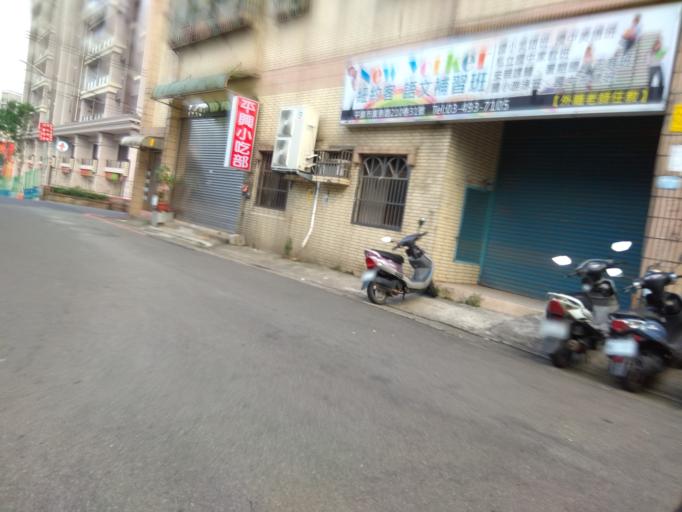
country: TW
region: Taiwan
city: Daxi
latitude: 24.9434
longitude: 121.2027
